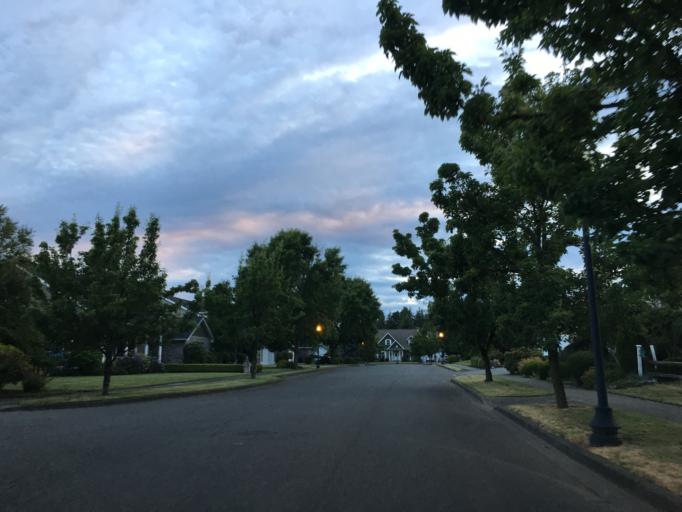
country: US
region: Washington
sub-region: Whatcom County
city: Lynden
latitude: 48.9557
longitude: -122.4441
